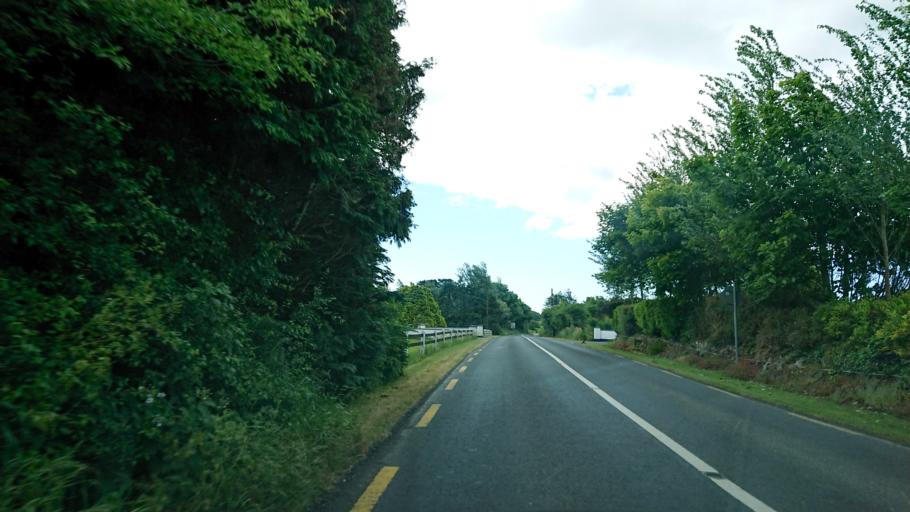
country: IE
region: Munster
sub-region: Waterford
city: Tra Mhor
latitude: 52.1820
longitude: -7.1718
